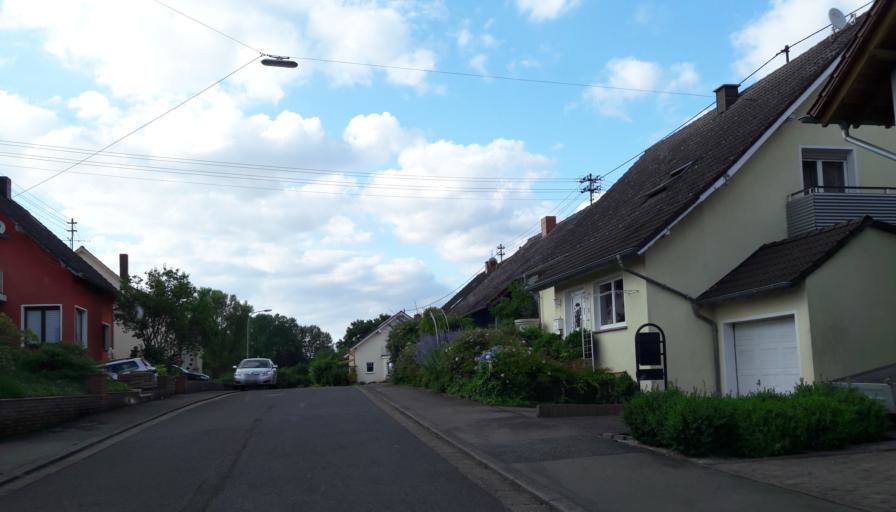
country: DE
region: Saarland
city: Mainzweiler
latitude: 49.4381
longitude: 7.1213
